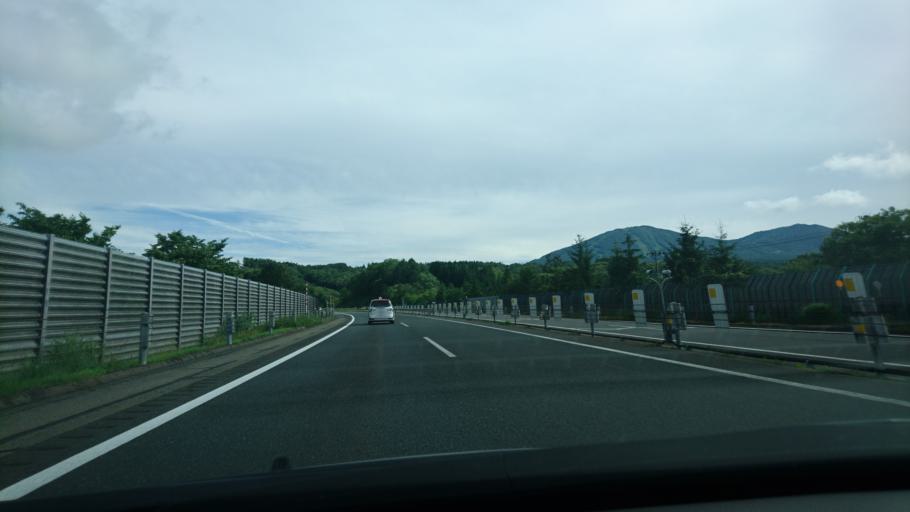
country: JP
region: Akita
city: Hanawa
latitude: 40.0254
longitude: 140.9829
